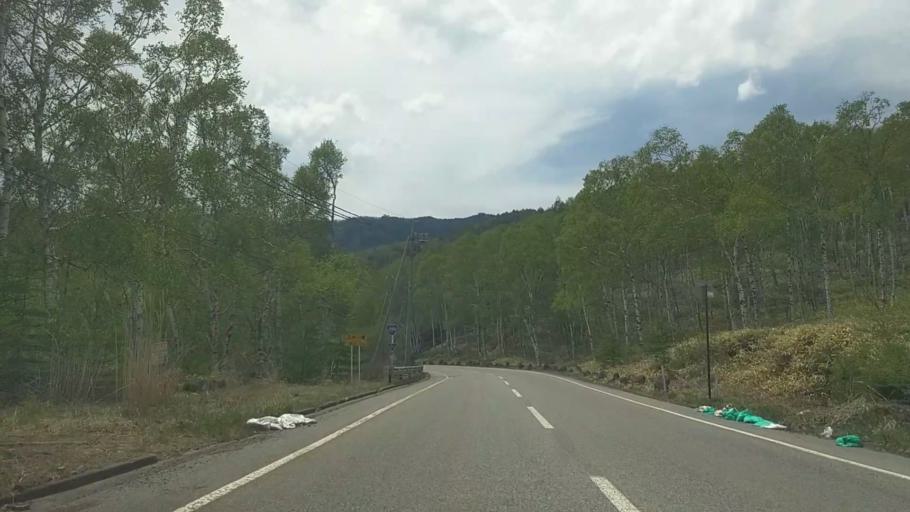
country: JP
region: Nagano
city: Saku
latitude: 36.0765
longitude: 138.3832
